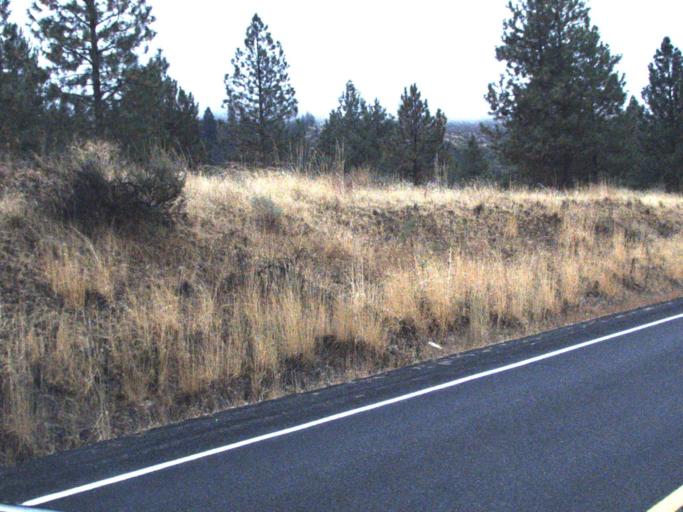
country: US
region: Washington
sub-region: Lincoln County
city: Davenport
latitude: 47.7859
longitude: -117.8894
